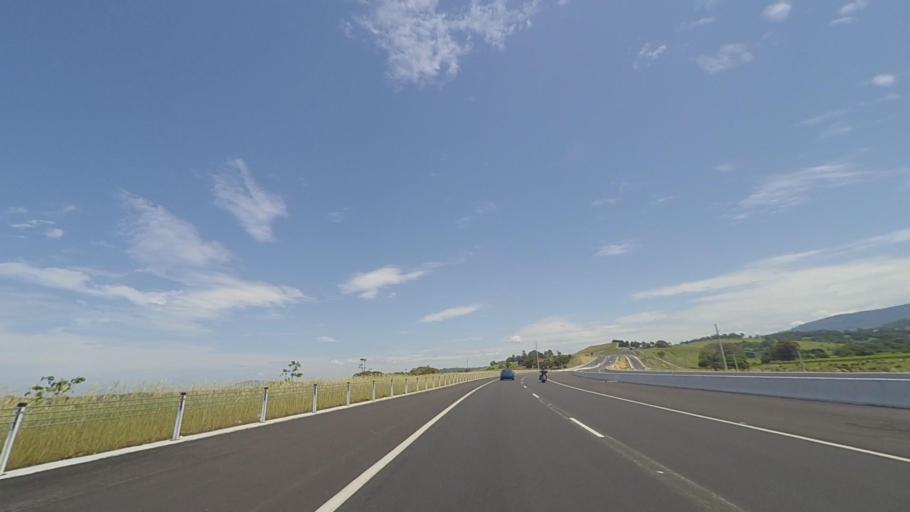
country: AU
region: New South Wales
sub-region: Kiama
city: Gerringong
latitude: -34.7453
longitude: 150.8150
